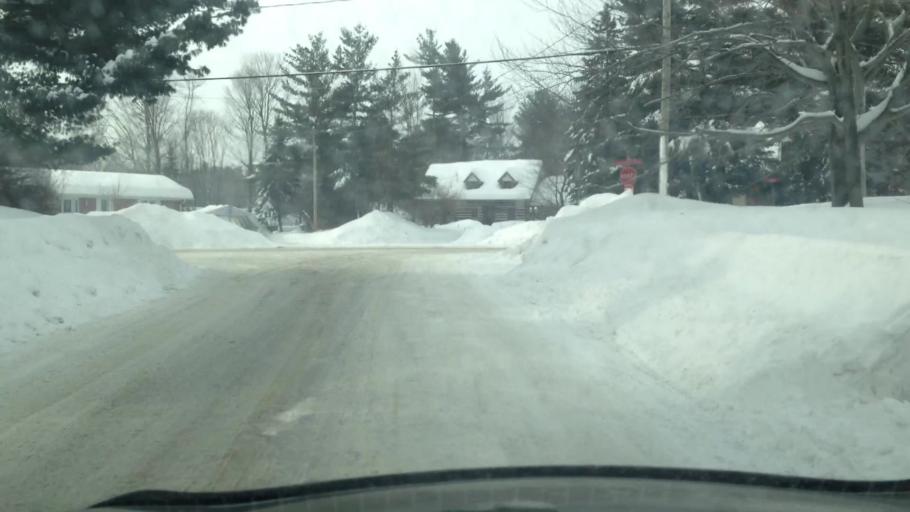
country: CA
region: Quebec
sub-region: Laurentides
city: Saint-Jerome
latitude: 45.7969
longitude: -74.0363
